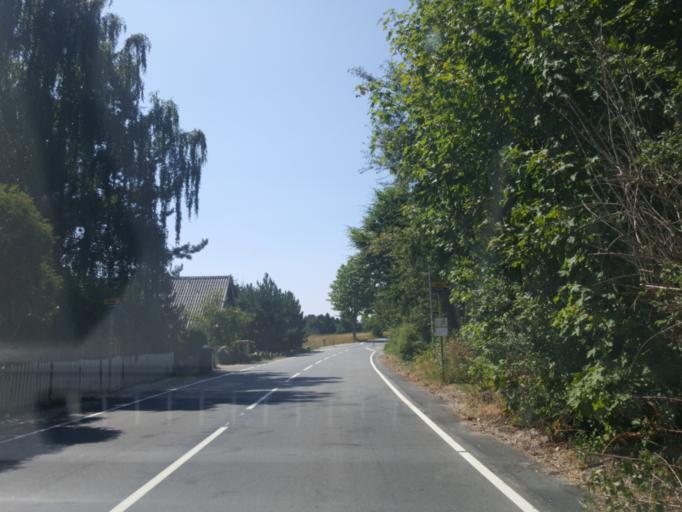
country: DK
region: Capital Region
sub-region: Fredensborg Kommune
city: Fredensborg
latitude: 55.9176
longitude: 12.4330
